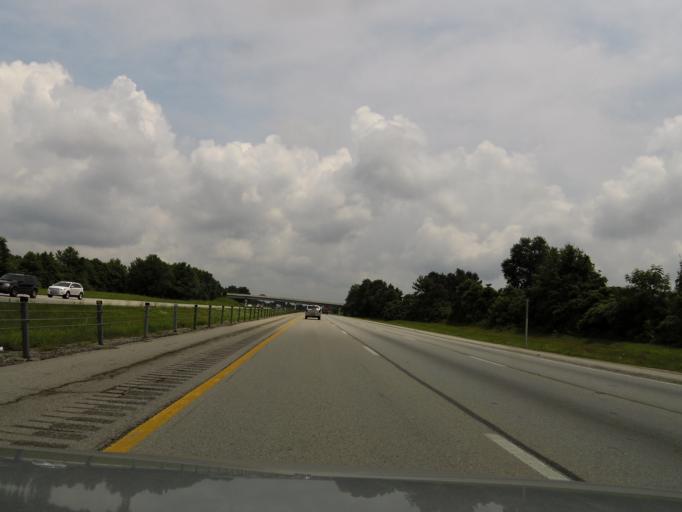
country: US
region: Kentucky
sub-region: Hardin County
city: Elizabethtown
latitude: 37.7259
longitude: -85.8224
